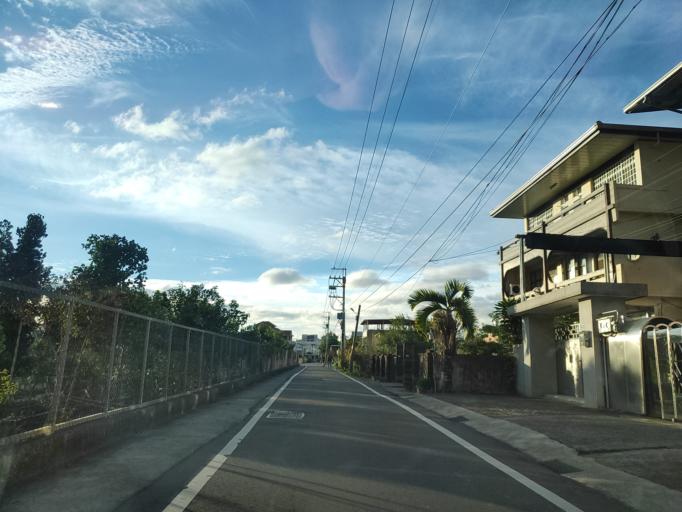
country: TW
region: Taiwan
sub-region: Miaoli
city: Miaoli
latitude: 24.5583
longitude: 120.8310
